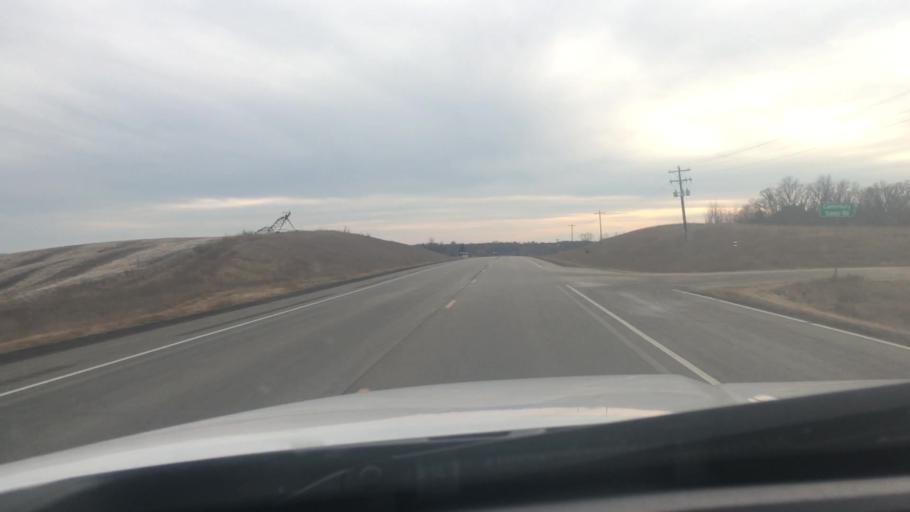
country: US
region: Minnesota
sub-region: Otter Tail County
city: Perham
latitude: 46.3073
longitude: -95.7183
